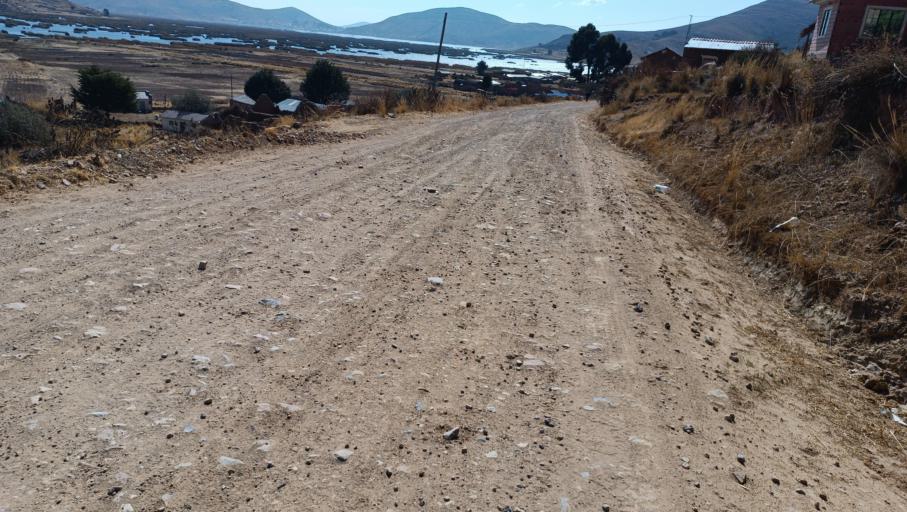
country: BO
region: La Paz
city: Huatajata
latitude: -16.3472
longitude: -68.6739
